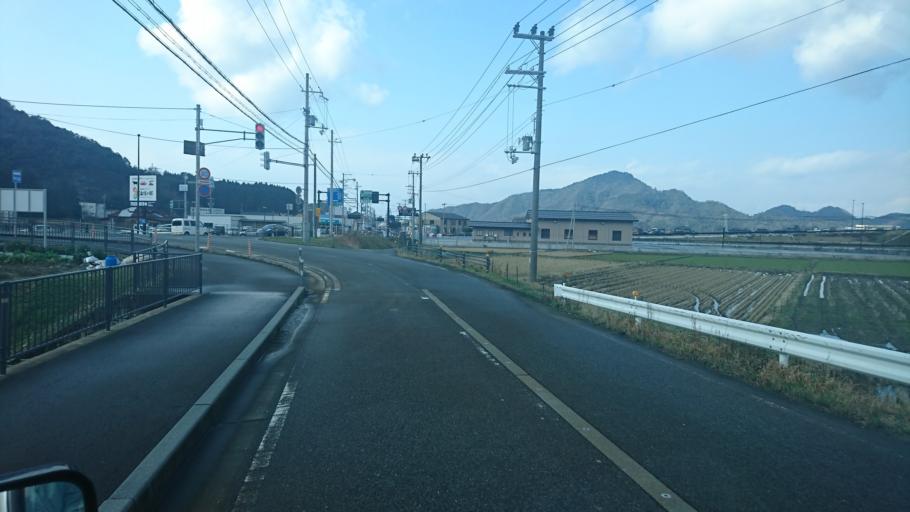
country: JP
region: Tottori
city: Tottori
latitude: 35.6100
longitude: 134.4708
